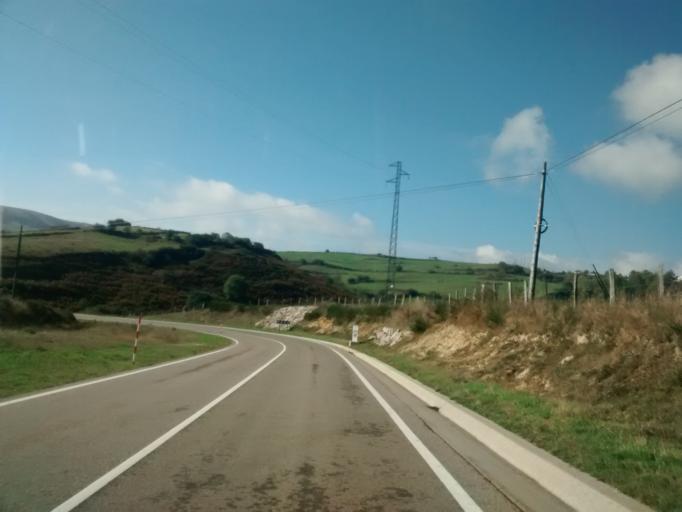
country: ES
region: Cantabria
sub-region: Provincia de Cantabria
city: Reinosa
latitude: 42.9859
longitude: -4.1060
